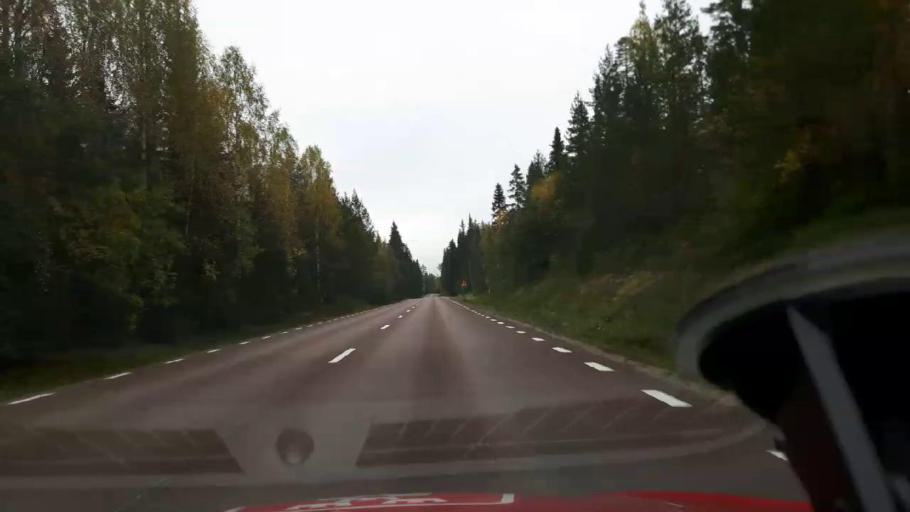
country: SE
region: Jaemtland
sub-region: Harjedalens Kommun
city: Sveg
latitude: 62.3325
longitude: 14.7339
